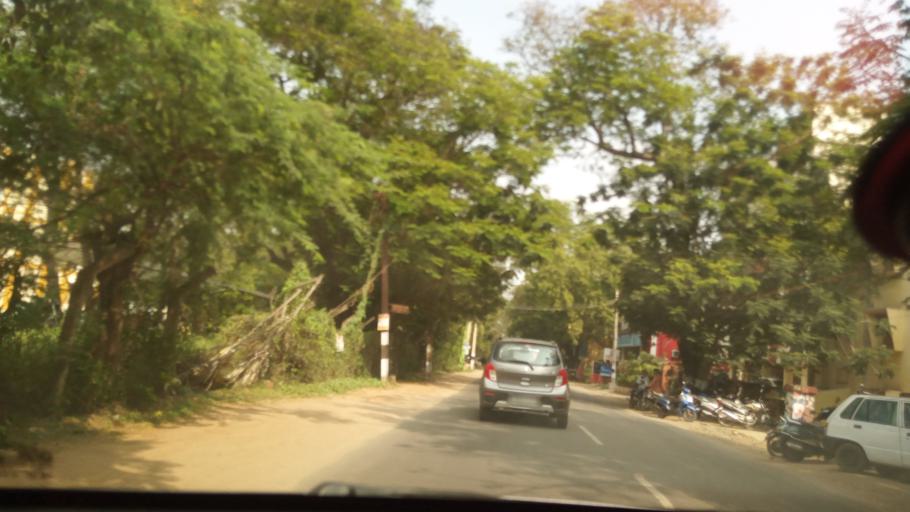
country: IN
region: Tamil Nadu
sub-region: Coimbatore
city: Coimbatore
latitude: 11.0147
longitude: 76.9454
